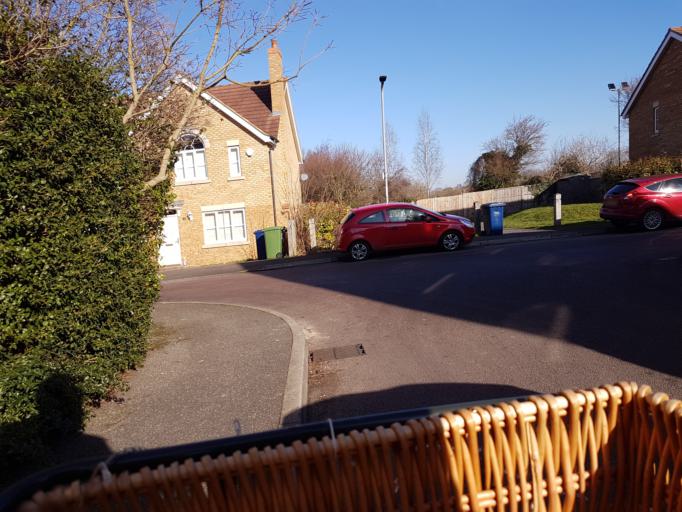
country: GB
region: England
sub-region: Cambridgeshire
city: Fulbourn
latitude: 52.1848
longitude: 0.1745
